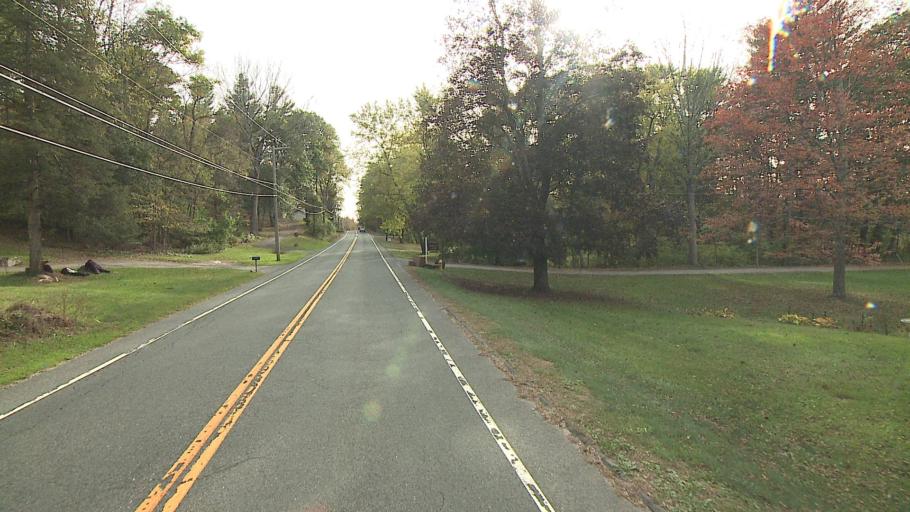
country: US
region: Connecticut
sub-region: Litchfield County
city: Canaan
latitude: 42.0113
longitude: -73.3537
